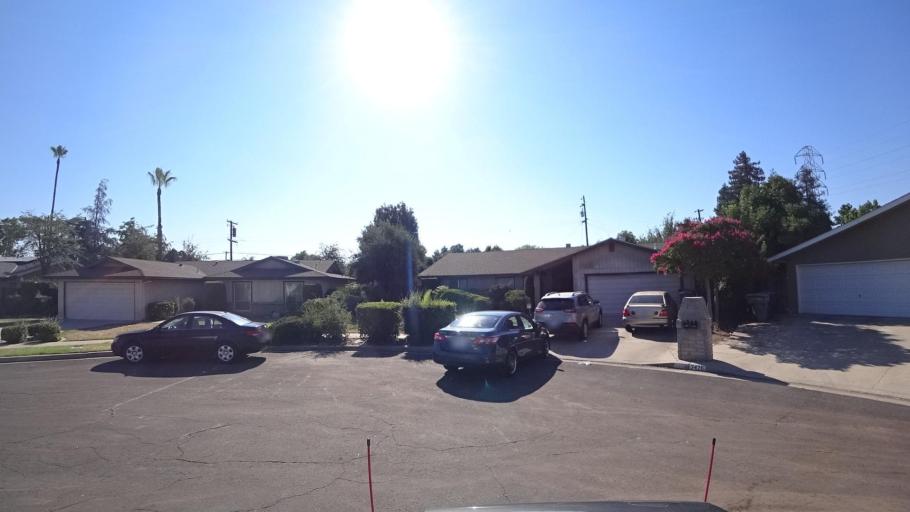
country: US
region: California
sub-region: Fresno County
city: Fresno
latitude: 36.7818
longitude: -119.7685
